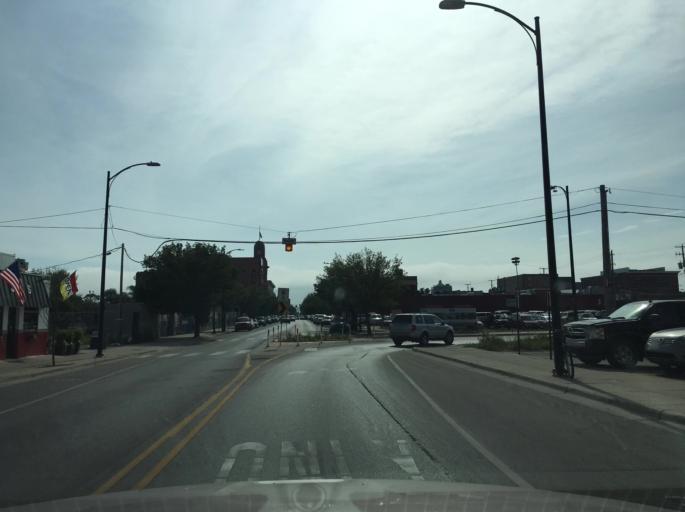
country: US
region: Michigan
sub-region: Grand Traverse County
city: Traverse City
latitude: 44.7641
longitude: -85.6267
